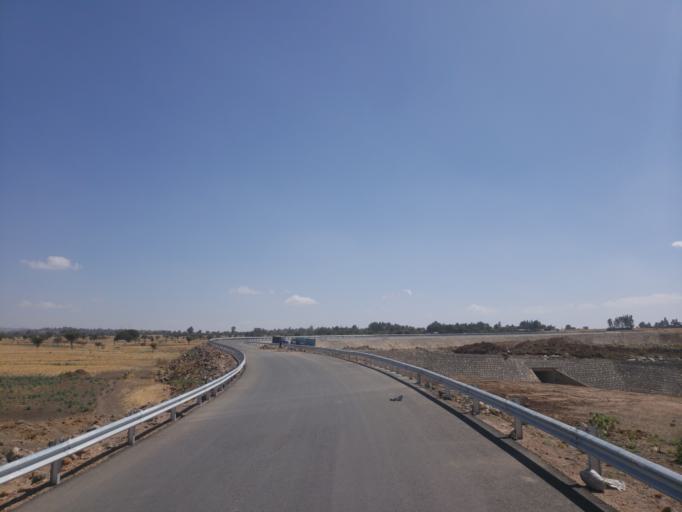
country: ET
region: Oromiya
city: Mojo
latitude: 8.5814
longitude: 39.1714
